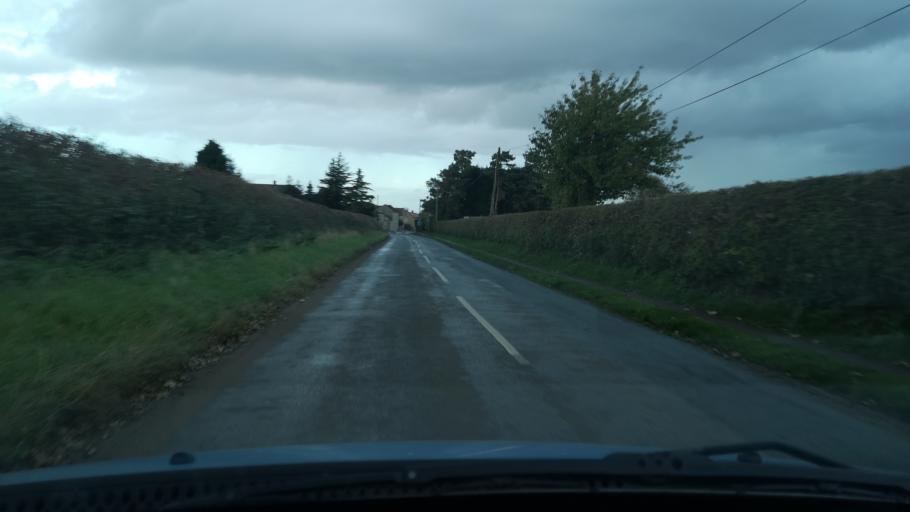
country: GB
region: England
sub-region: Doncaster
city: Norton
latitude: 53.6406
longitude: -1.2187
